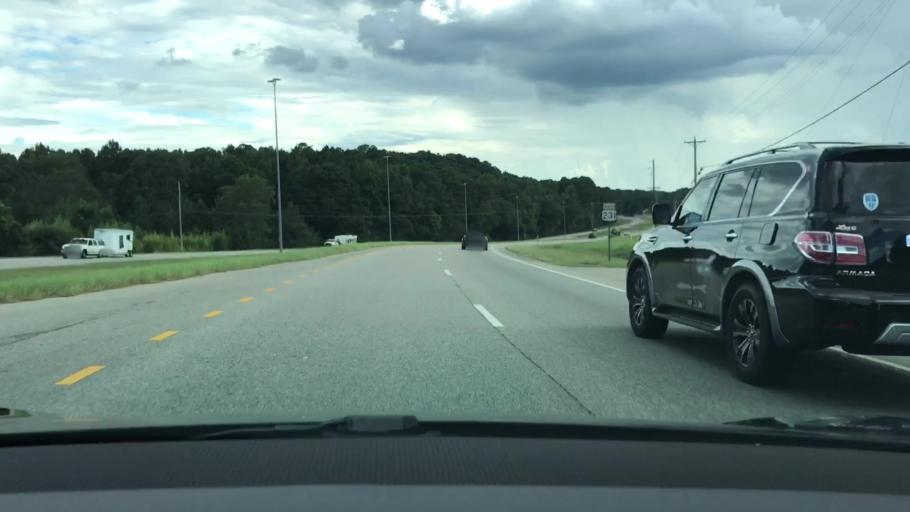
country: US
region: Alabama
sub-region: Pike County
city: Troy
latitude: 31.8326
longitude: -85.9912
